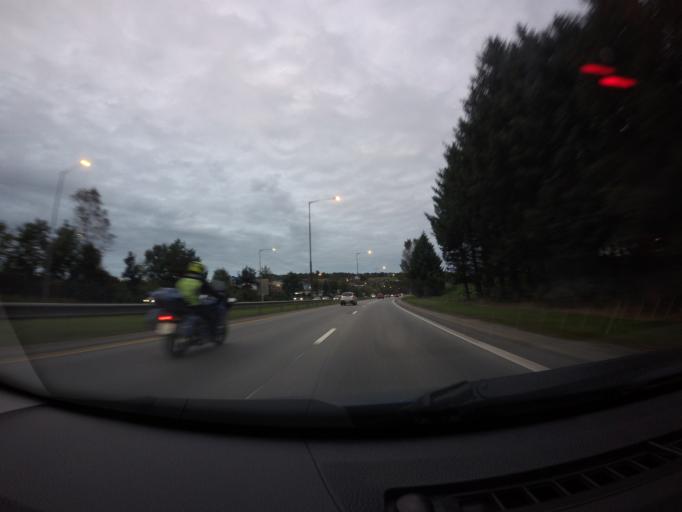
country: NO
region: Rogaland
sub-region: Stavanger
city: Stavanger
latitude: 58.9394
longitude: 5.7234
